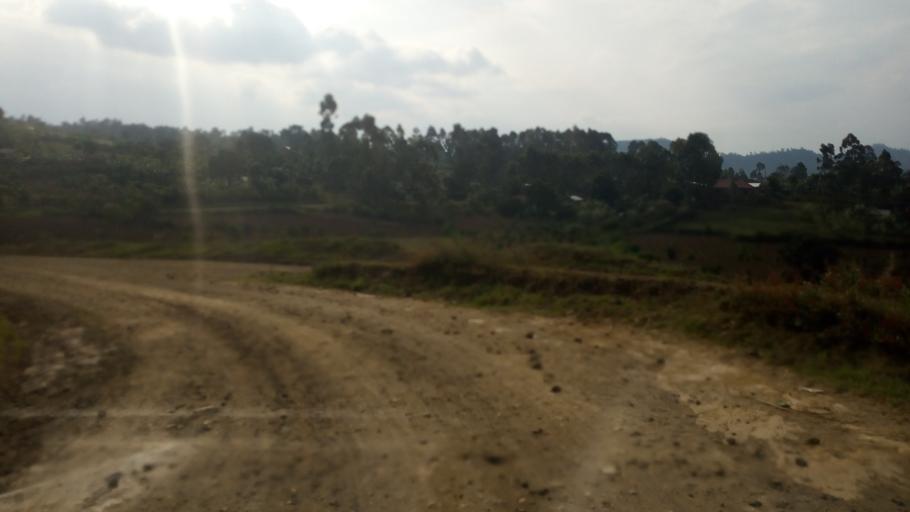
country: UG
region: Western Region
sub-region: Kisoro District
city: Kisoro
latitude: -1.2980
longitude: 29.7022
